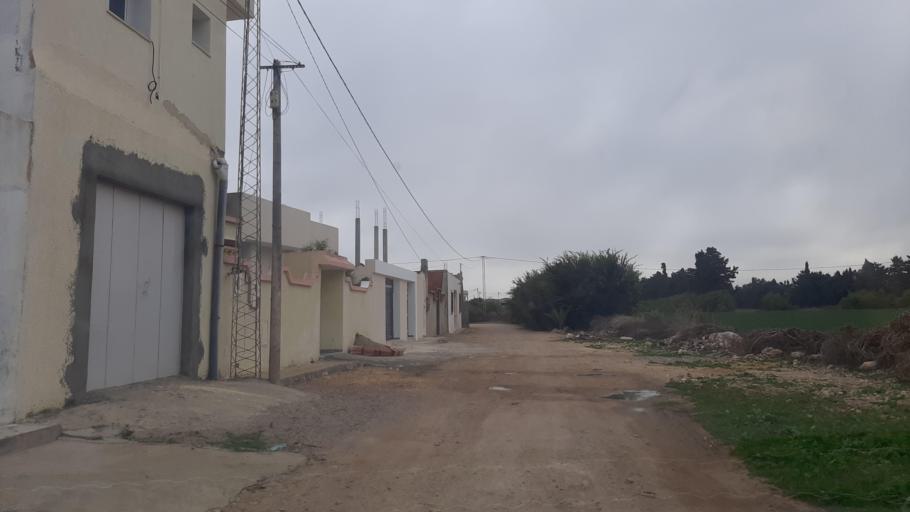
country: TN
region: Nabul
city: Menzel Heurr
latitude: 36.6843
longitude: 10.9282
